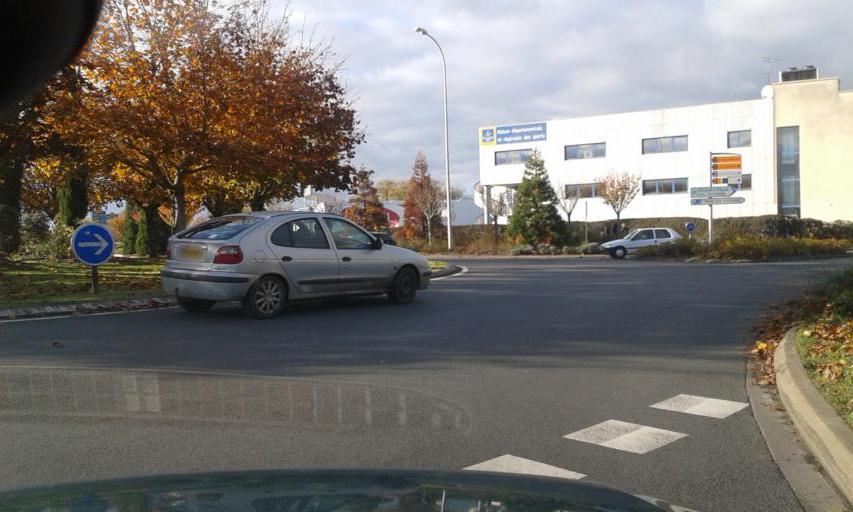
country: FR
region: Centre
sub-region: Departement du Loiret
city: Olivet
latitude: 47.8453
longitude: 1.9170
